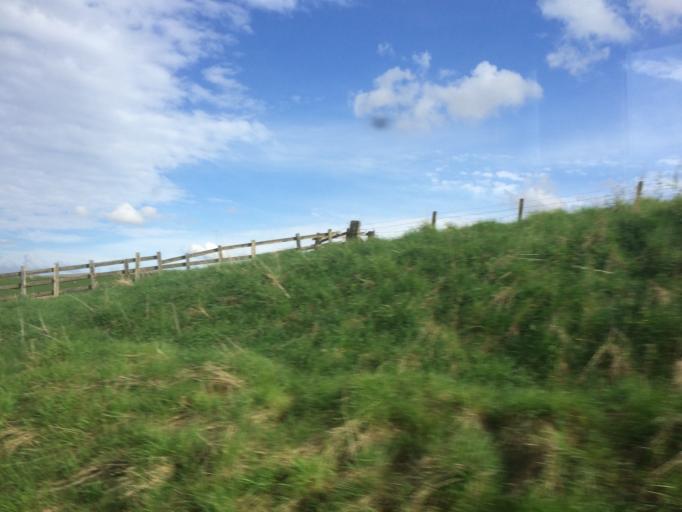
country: GB
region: Scotland
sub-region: Clackmannanshire
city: Alva
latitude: 56.2612
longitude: -3.8207
